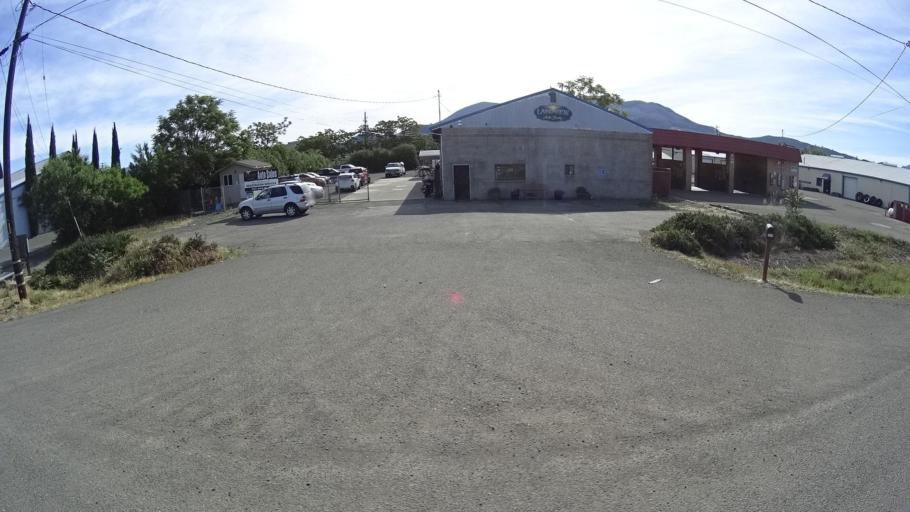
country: US
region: California
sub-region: Lake County
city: Kelseyville
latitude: 38.9808
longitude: -122.8455
